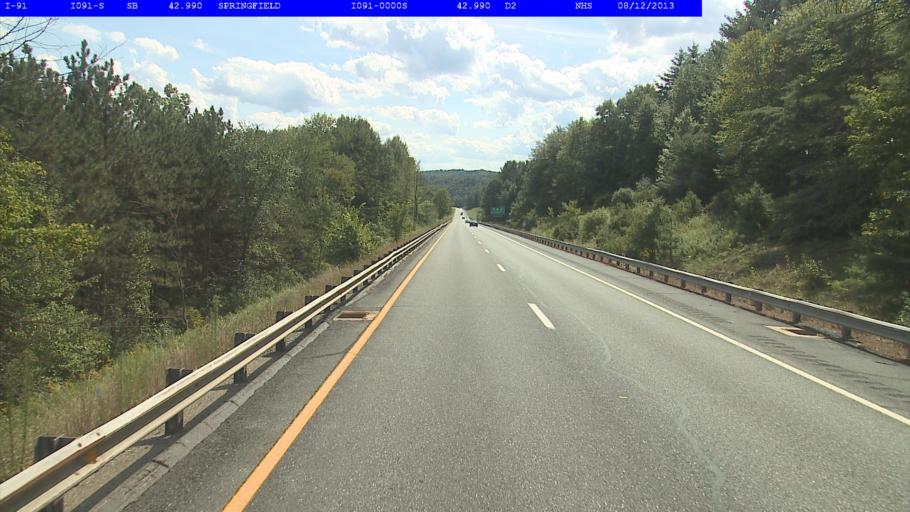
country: US
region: New Hampshire
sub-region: Sullivan County
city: Charlestown
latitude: 43.2844
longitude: -72.4294
